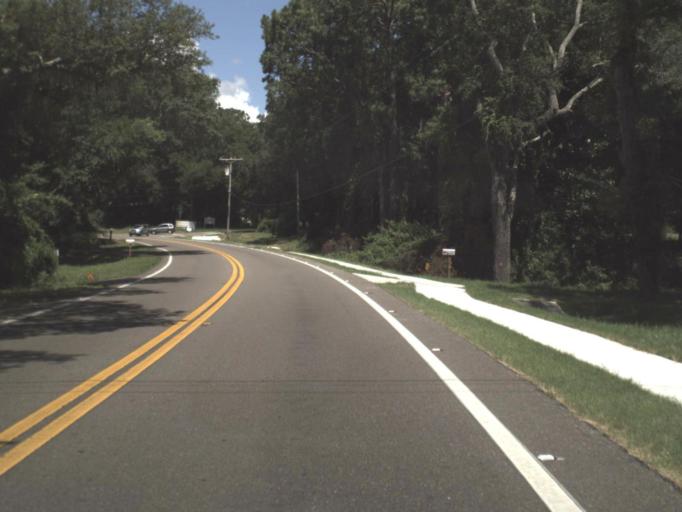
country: US
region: Florida
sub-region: Clay County
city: Keystone Heights
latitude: 29.7762
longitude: -82.0467
